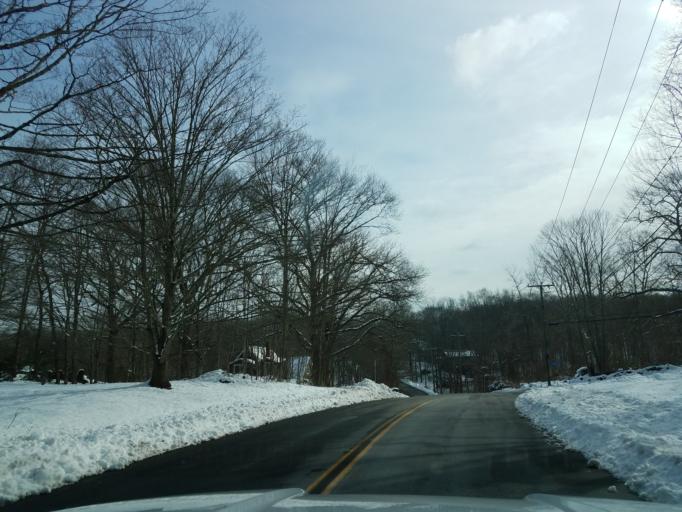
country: US
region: Connecticut
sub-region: Middlesex County
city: Lake Pocotopaug
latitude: 41.6072
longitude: -72.4906
